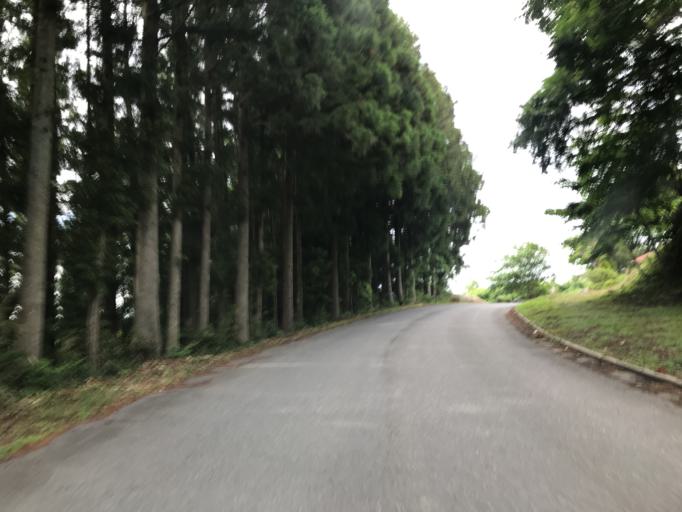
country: JP
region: Fukushima
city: Funehikimachi-funehiki
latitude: 37.5118
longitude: 140.5661
